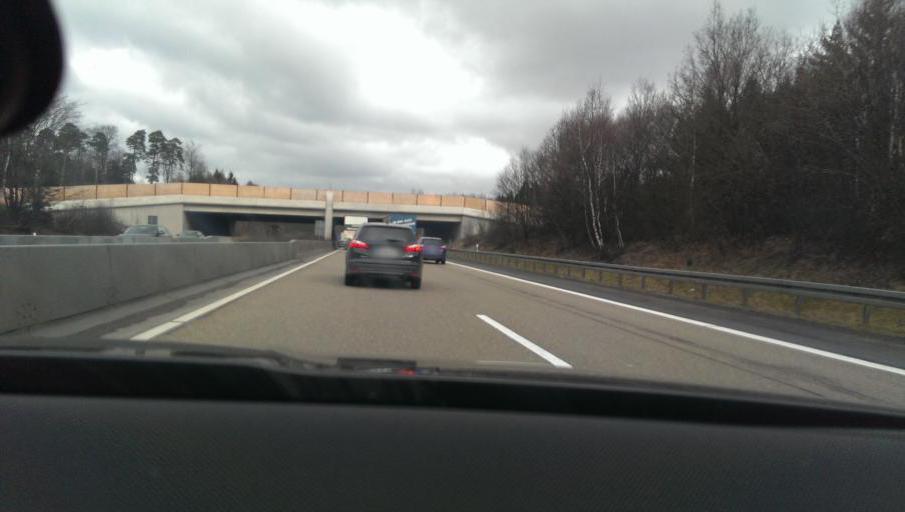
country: DE
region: Hesse
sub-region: Regierungsbezirk Kassel
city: Burghaun
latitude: 50.6364
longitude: 9.6797
